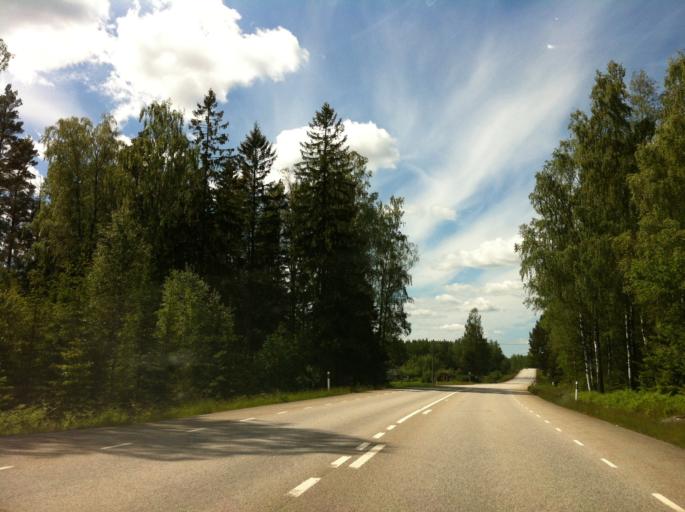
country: SE
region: Vaestra Goetaland
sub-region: Amals Kommun
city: Amal
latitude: 58.9907
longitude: 12.6702
